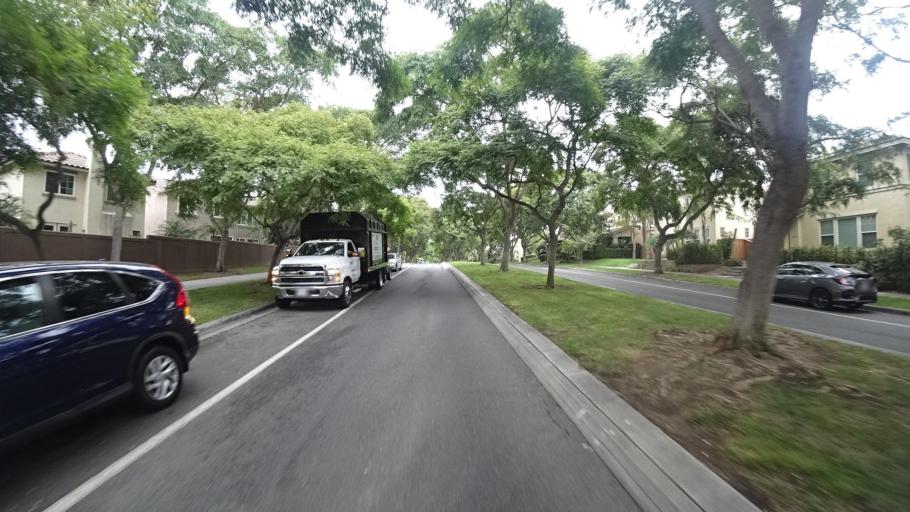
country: US
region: California
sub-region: San Diego County
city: Fairbanks Ranch
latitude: 33.0125
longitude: -117.1158
